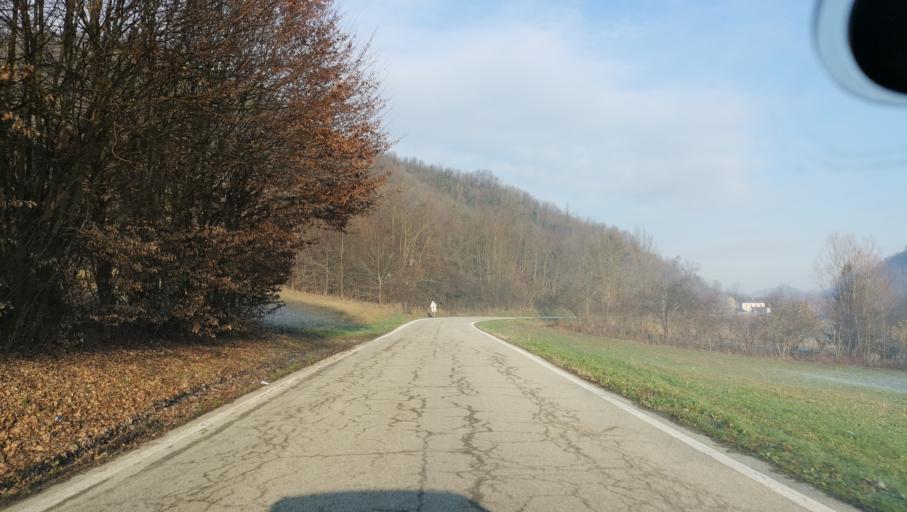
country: IT
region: Piedmont
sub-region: Provincia di Asti
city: Berzano di San Pietro
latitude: 45.1080
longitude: 7.9417
